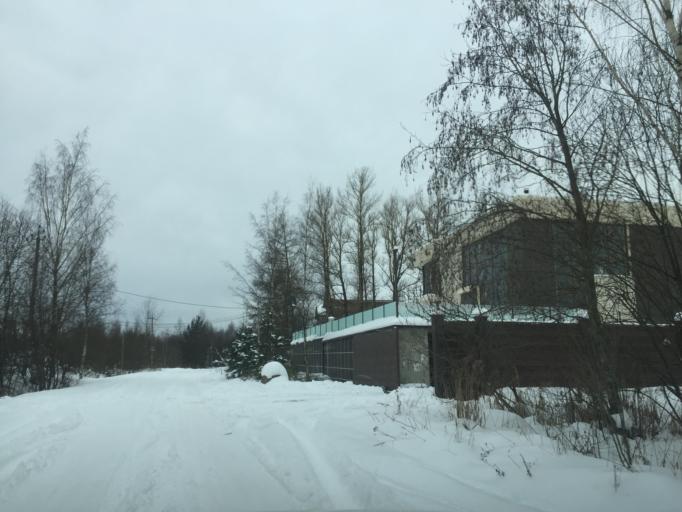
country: RU
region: Leningrad
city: Otradnoye
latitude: 59.7849
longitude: 30.7884
